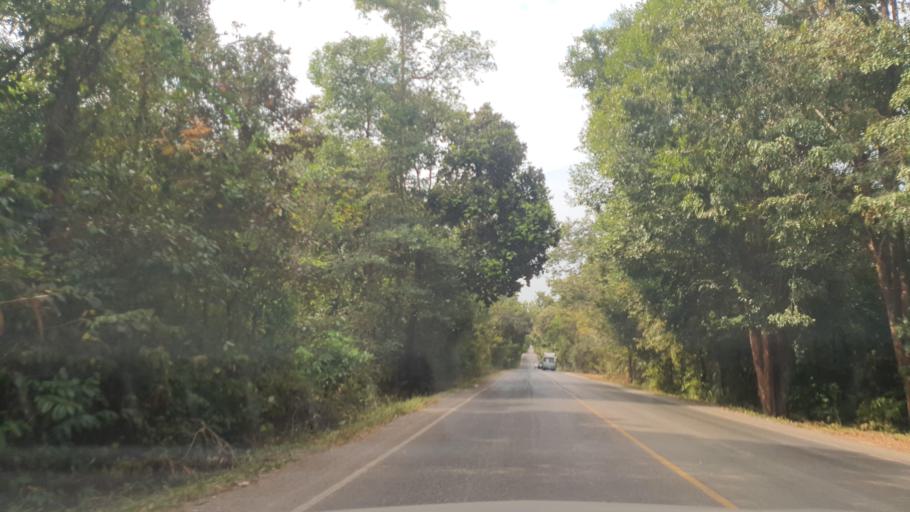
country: TH
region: Changwat Bueng Kan
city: Bung Khla
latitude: 18.2939
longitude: 103.9237
